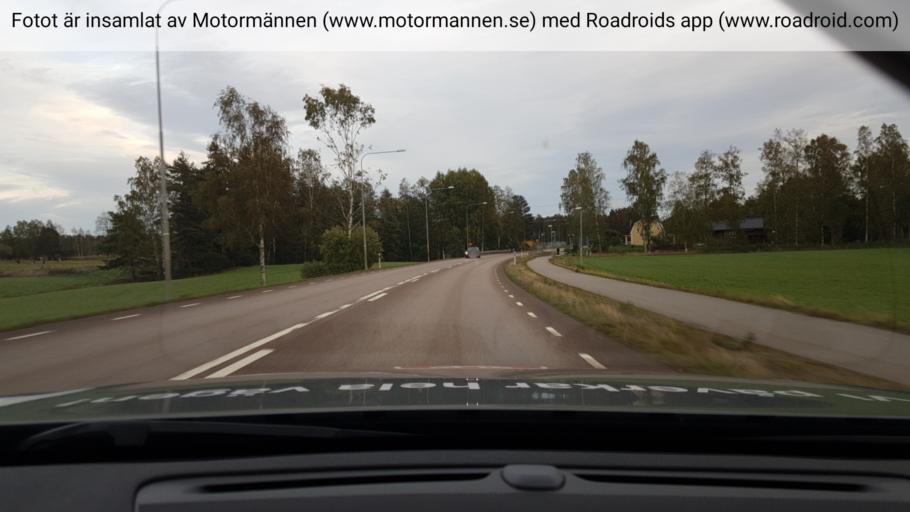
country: SE
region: Vaestra Goetaland
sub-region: Amals Kommun
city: Amal
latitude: 59.0570
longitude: 12.6669
